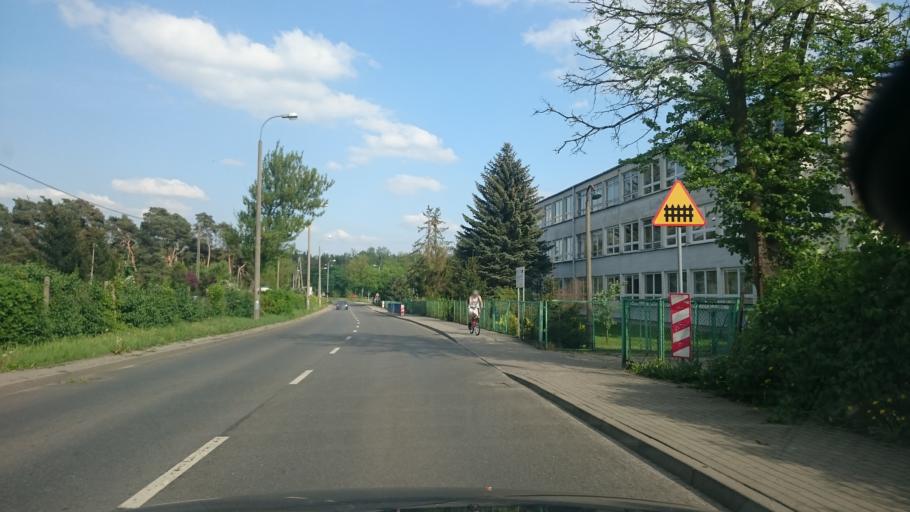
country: PL
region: Kujawsko-Pomorskie
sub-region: Grudziadz
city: Grudziadz
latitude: 53.4638
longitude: 18.7431
